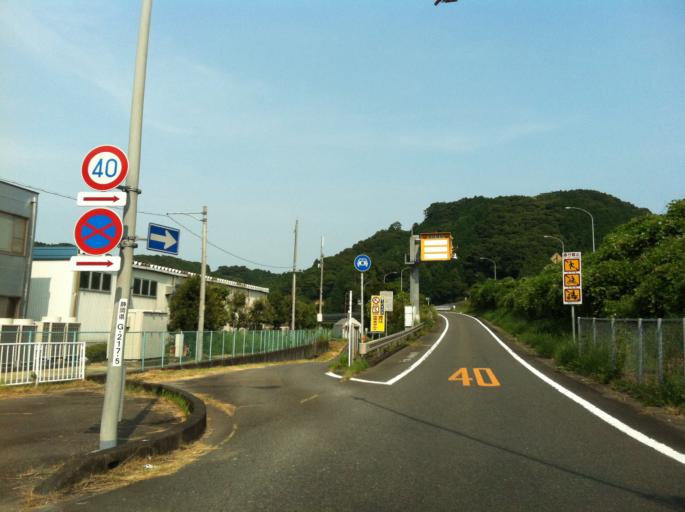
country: JP
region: Shizuoka
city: Shimada
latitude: 34.8483
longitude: 138.1828
